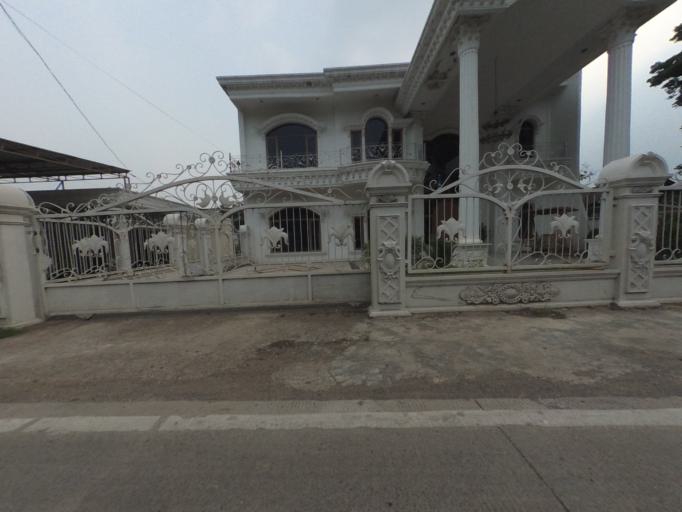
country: ID
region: West Java
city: Sidoger Lebak
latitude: -6.5651
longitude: 106.5883
